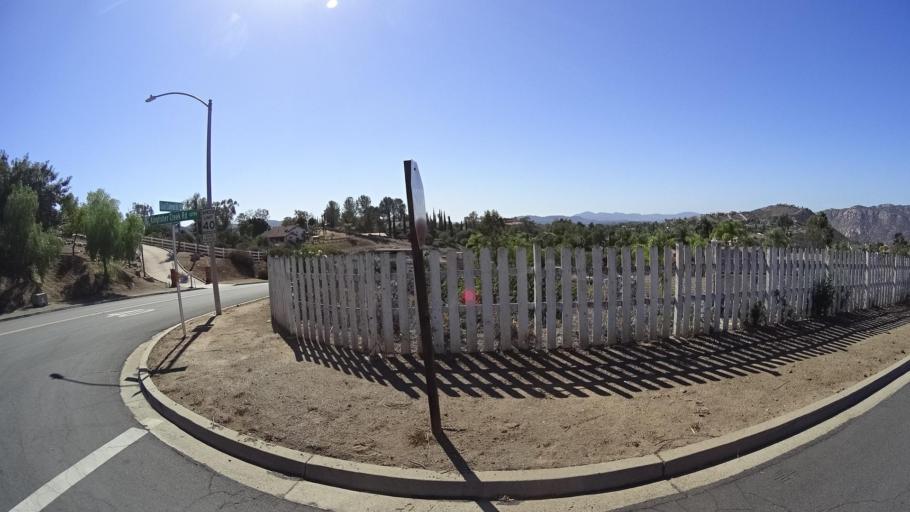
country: US
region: California
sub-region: San Diego County
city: Harbison Canyon
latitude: 32.8699
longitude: -116.8514
